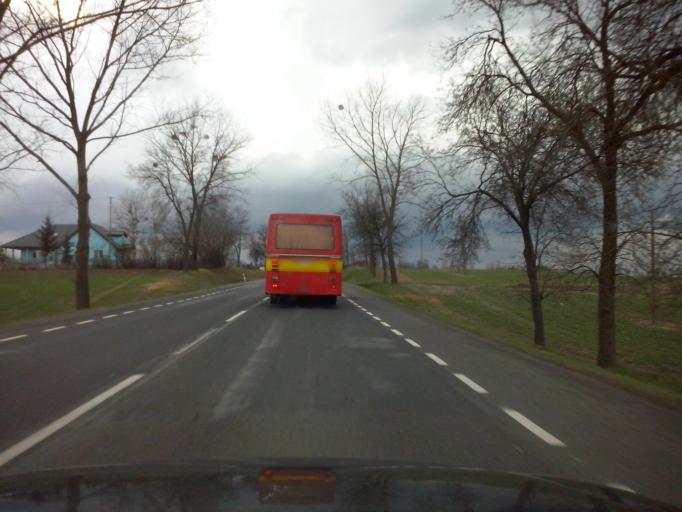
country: PL
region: Lublin Voivodeship
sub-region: Powiat chelmski
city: Rejowiec Fabryczny
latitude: 51.1734
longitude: 23.2776
